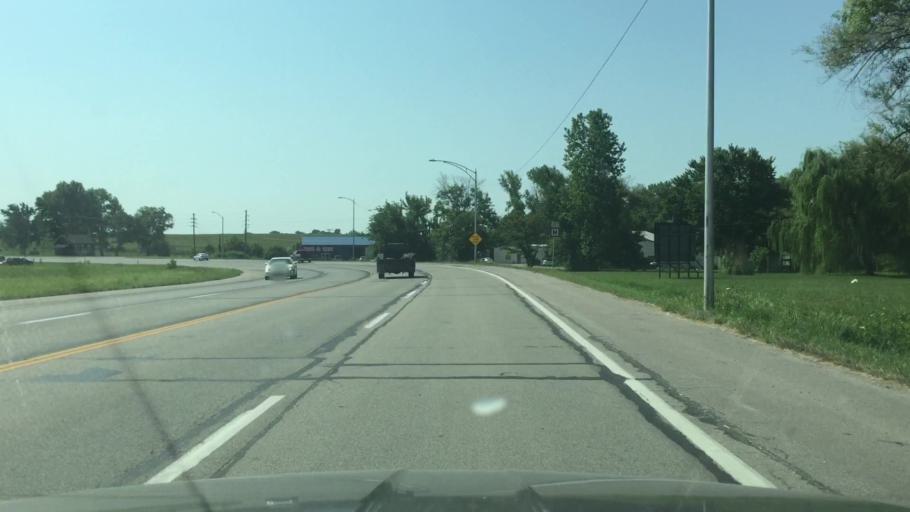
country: US
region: Missouri
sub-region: Pettis County
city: Sedalia
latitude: 38.7013
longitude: -93.1924
